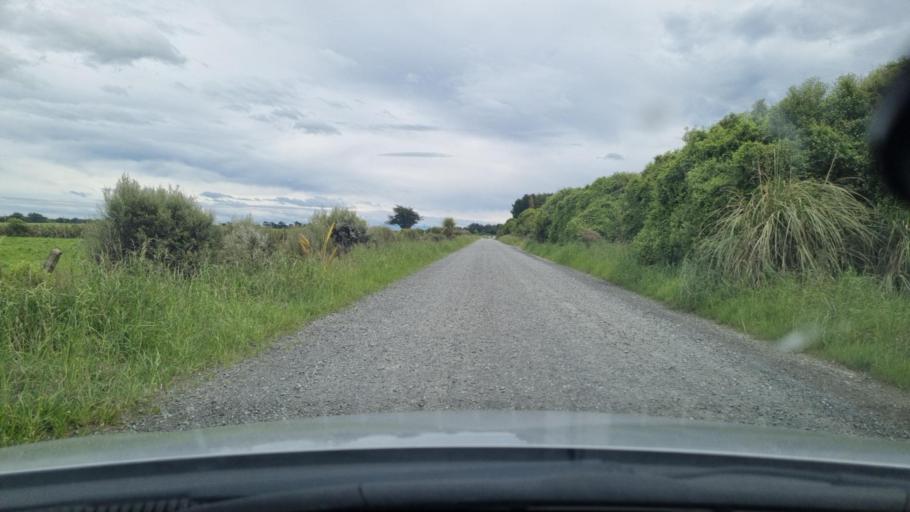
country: NZ
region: Southland
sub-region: Invercargill City
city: Invercargill
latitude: -46.4054
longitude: 168.2775
